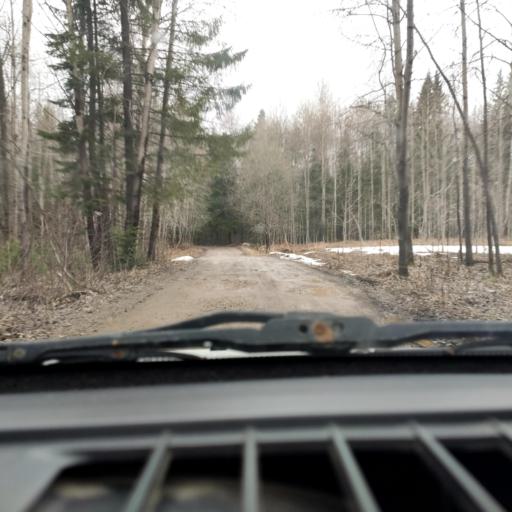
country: RU
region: Perm
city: Kultayevo
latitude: 57.8218
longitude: 55.7977
